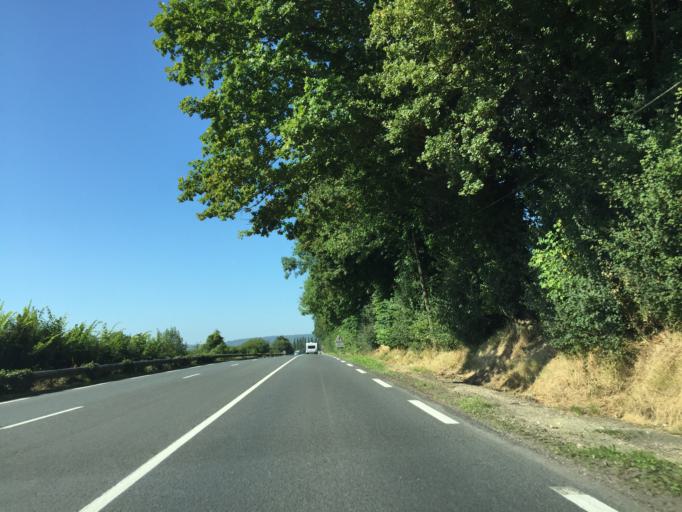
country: FR
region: Lower Normandy
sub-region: Departement du Calvados
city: Lisieux
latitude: 49.2467
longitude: 0.2211
